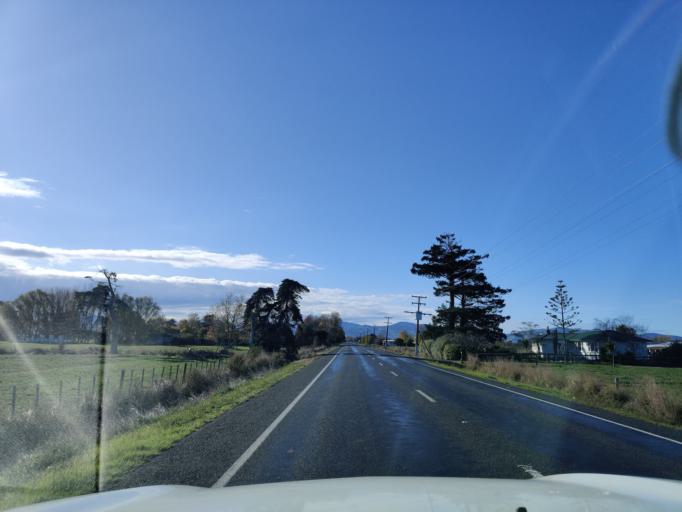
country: NZ
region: Waikato
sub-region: Hauraki District
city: Ngatea
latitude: -37.3112
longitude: 175.5739
